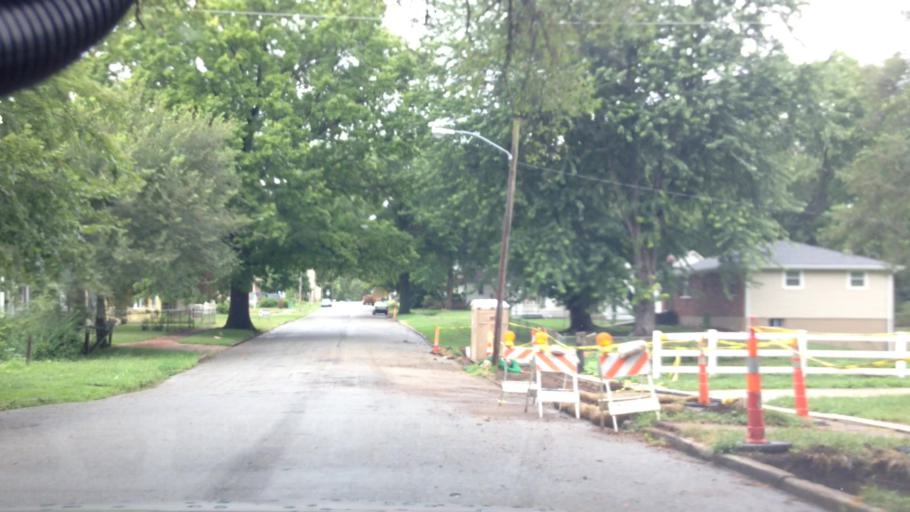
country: US
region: Kansas
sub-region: Leavenworth County
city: Leavenworth
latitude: 39.3213
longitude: -94.9258
